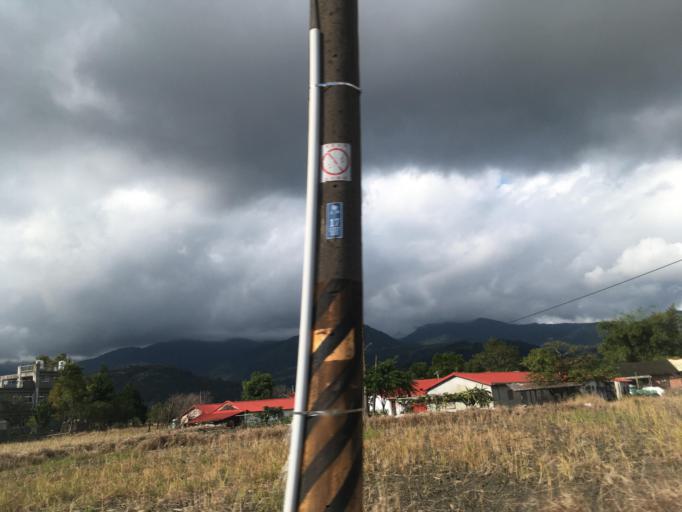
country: TW
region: Taiwan
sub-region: Yilan
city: Yilan
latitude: 24.6638
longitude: 121.6195
